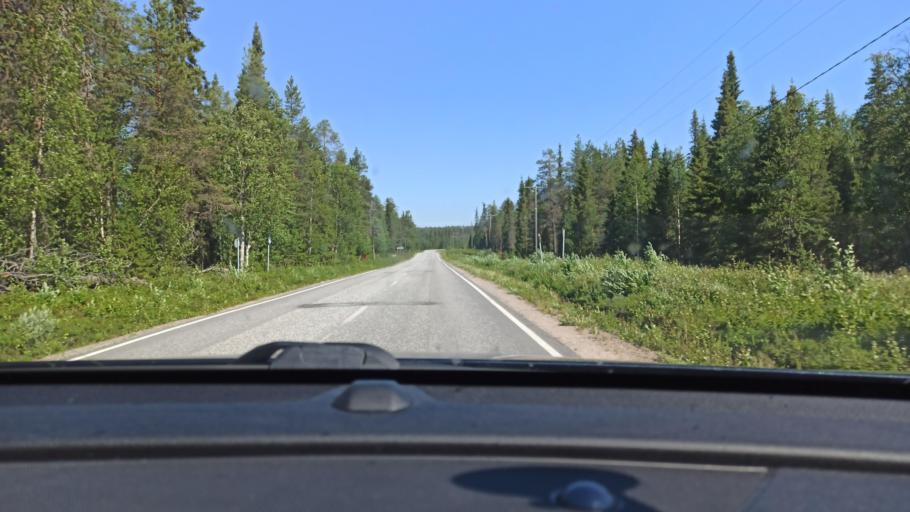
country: FI
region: Lapland
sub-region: Tunturi-Lappi
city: Kolari
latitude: 67.6261
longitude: 24.1554
